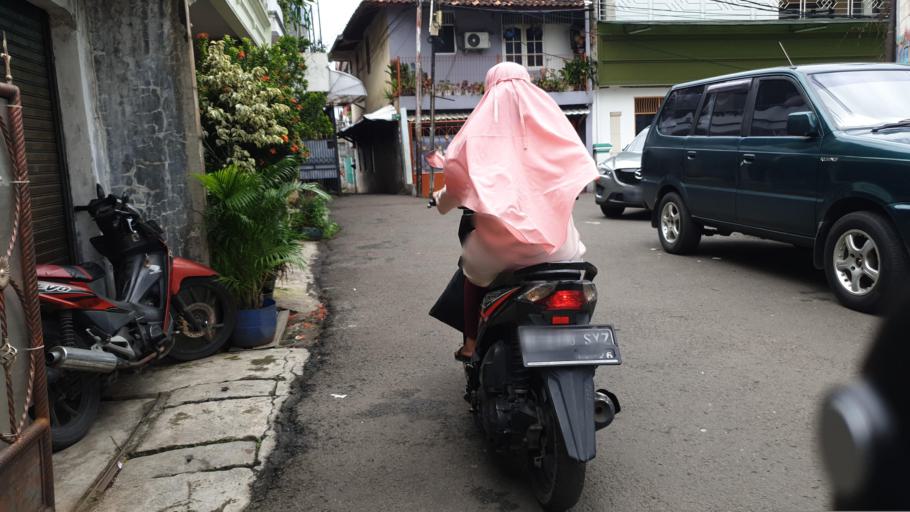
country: ID
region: Jakarta Raya
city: Jakarta
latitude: -6.2471
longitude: 106.7864
